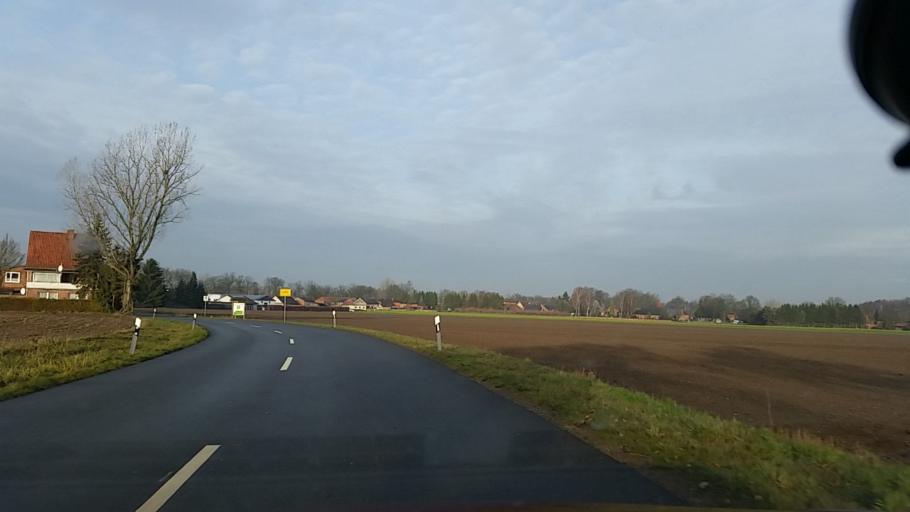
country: DE
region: Lower Saxony
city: Luder
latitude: 52.8052
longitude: 10.6711
